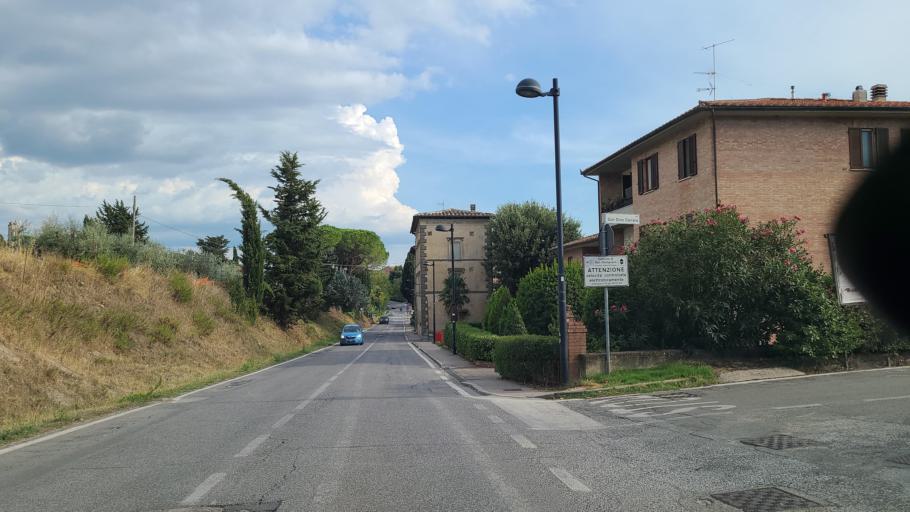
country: IT
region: Tuscany
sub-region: Provincia di Siena
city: San Gimignano
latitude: 43.4745
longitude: 11.0310
